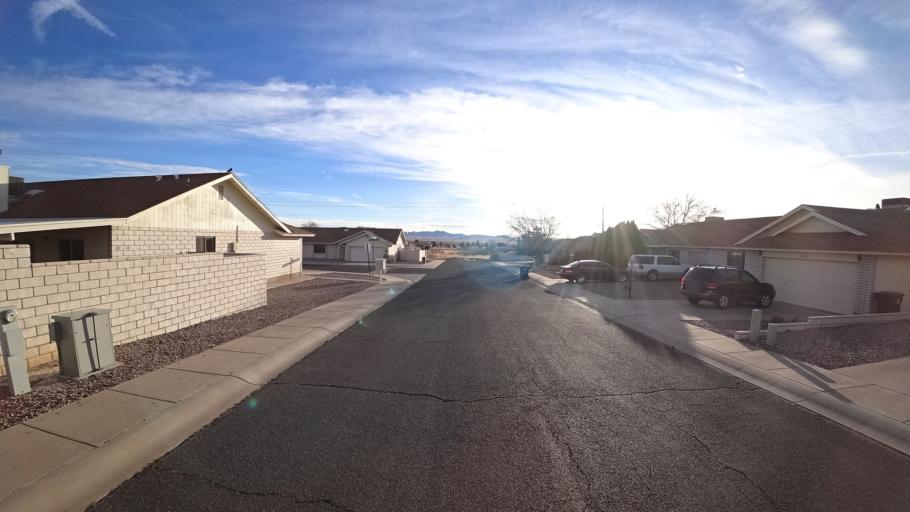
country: US
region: Arizona
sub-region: Mohave County
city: New Kingman-Butler
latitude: 35.2417
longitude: -114.0410
